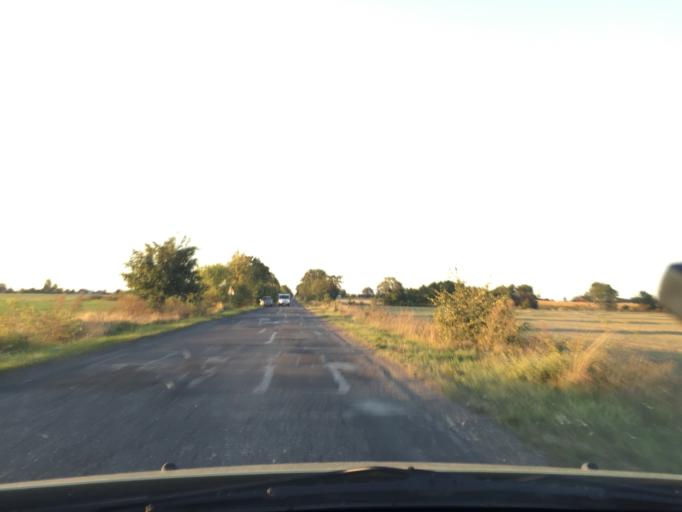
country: PL
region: Greater Poland Voivodeship
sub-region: Powiat pleszewski
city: Dobrzyca
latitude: 51.8349
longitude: 17.6206
